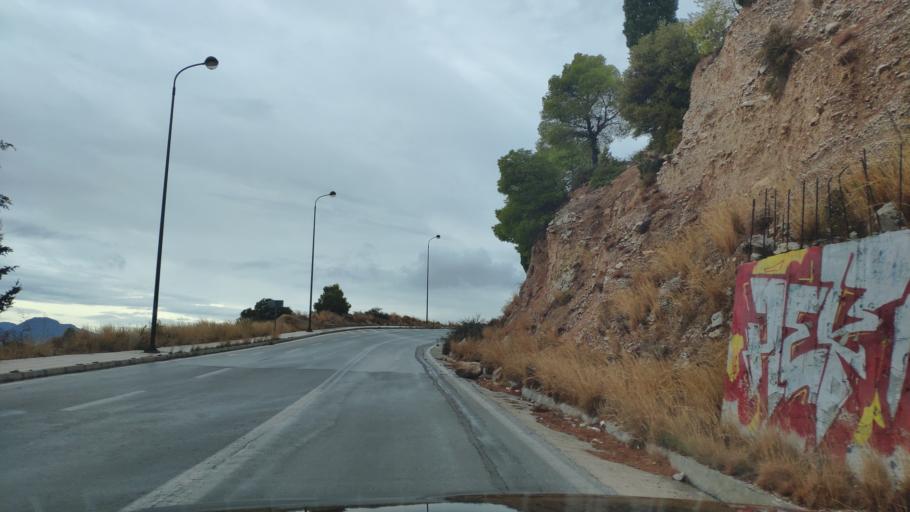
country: GR
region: Peloponnese
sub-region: Nomos Korinthias
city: Loutraki
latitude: 37.9828
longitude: 22.9767
